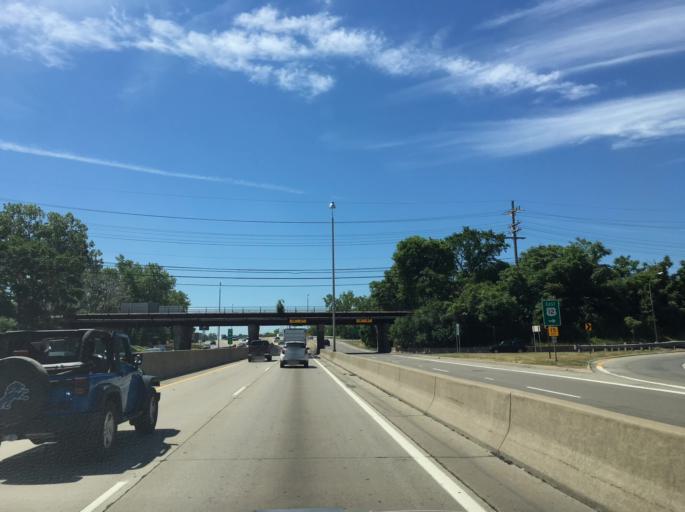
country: US
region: Michigan
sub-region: Wayne County
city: Dearborn
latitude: 42.3106
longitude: -83.2151
